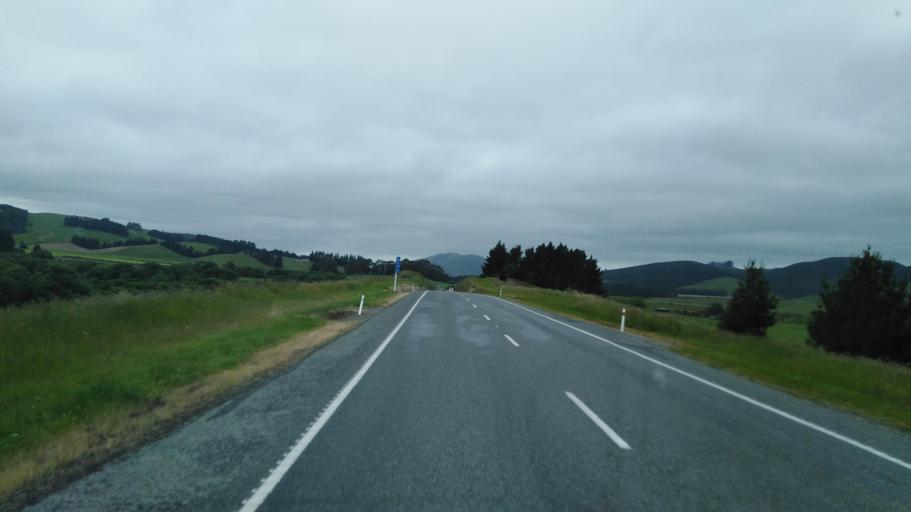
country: NZ
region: Canterbury
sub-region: Hurunui District
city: Amberley
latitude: -42.9555
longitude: 173.0054
